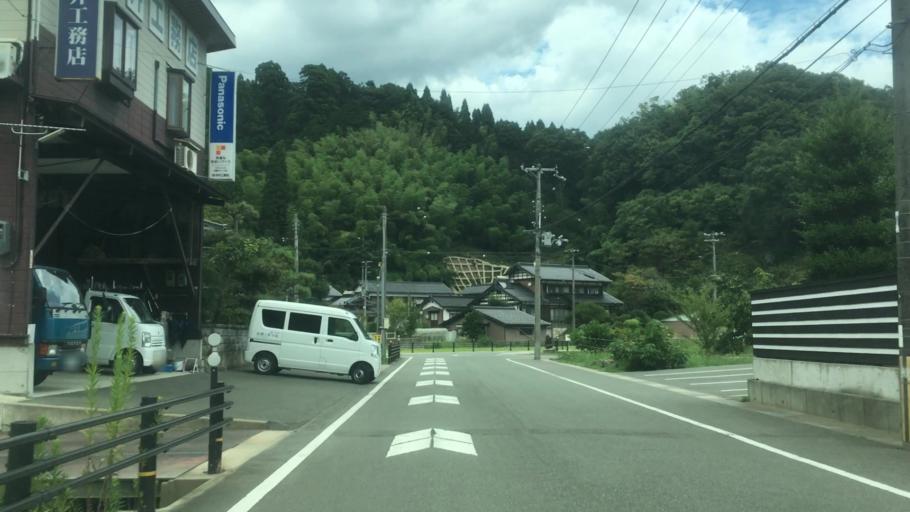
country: JP
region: Hyogo
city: Toyooka
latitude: 35.5932
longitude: 134.7987
